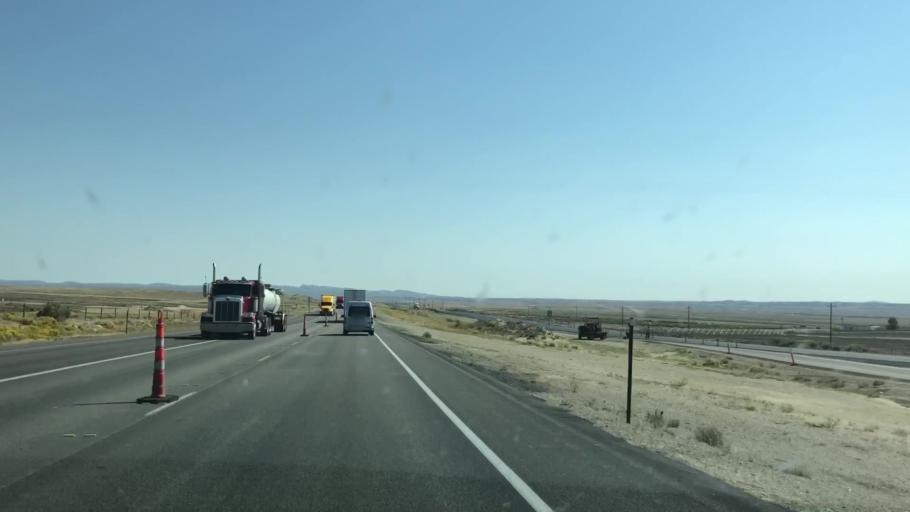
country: US
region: Wyoming
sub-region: Carbon County
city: Rawlins
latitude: 41.7508
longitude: -107.5644
